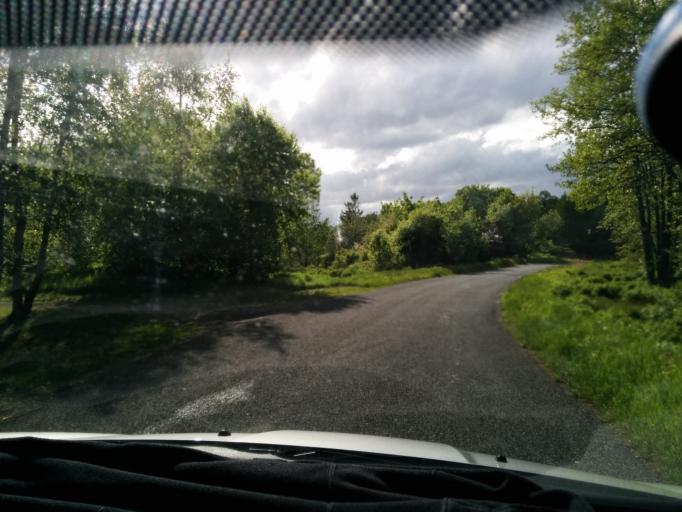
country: EE
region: Harju
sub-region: Loksa linn
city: Loksa
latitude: 59.6148
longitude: 25.6927
